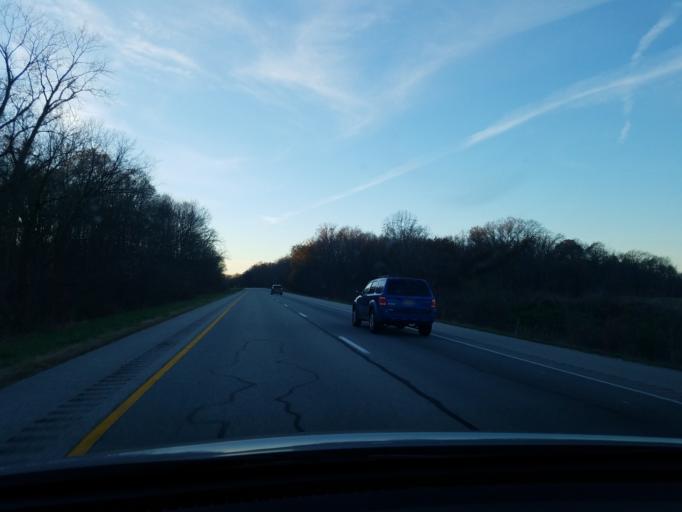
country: US
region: Indiana
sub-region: Posey County
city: Poseyville
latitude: 38.1935
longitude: -87.8407
